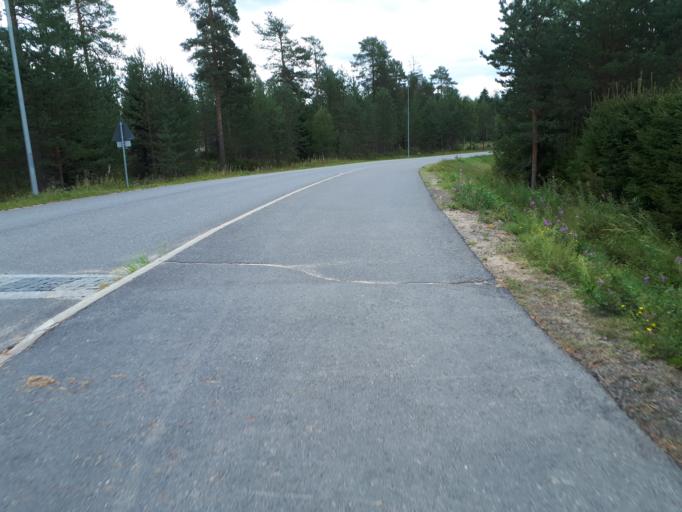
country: FI
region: Northern Ostrobothnia
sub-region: Oulunkaari
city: Ii
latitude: 65.3244
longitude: 25.4093
